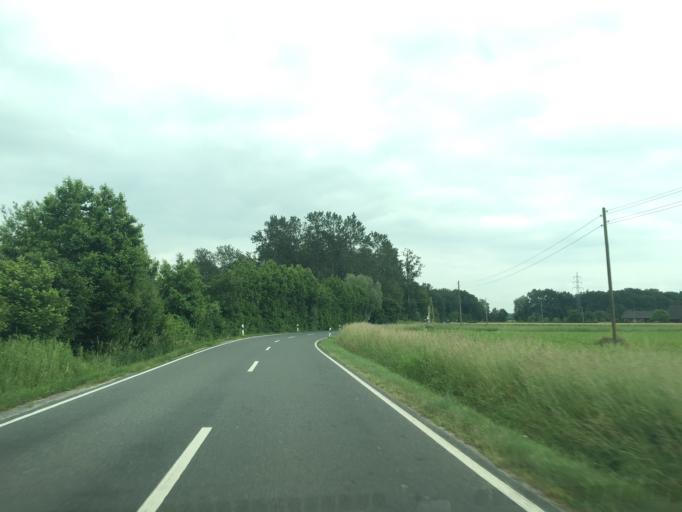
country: DE
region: North Rhine-Westphalia
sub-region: Regierungsbezirk Munster
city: Laer
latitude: 52.0793
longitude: 7.3482
